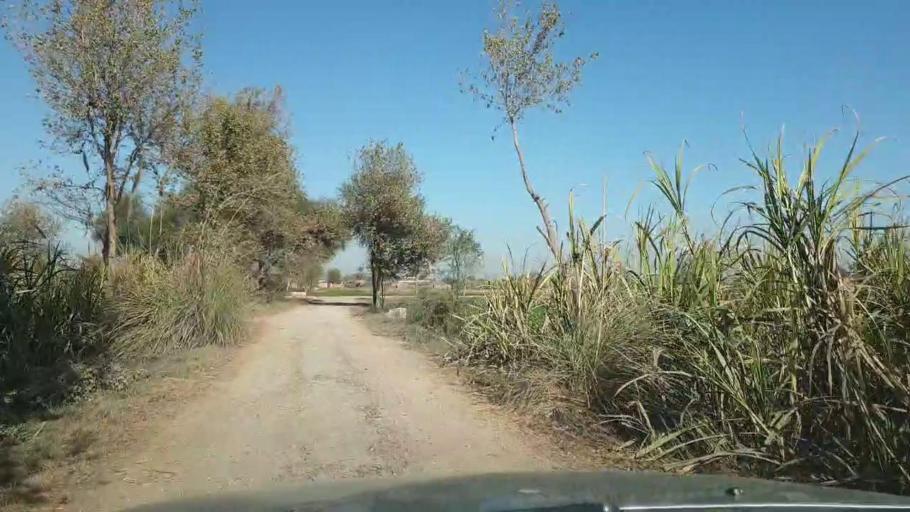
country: PK
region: Sindh
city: Ghotki
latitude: 28.0368
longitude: 69.2774
